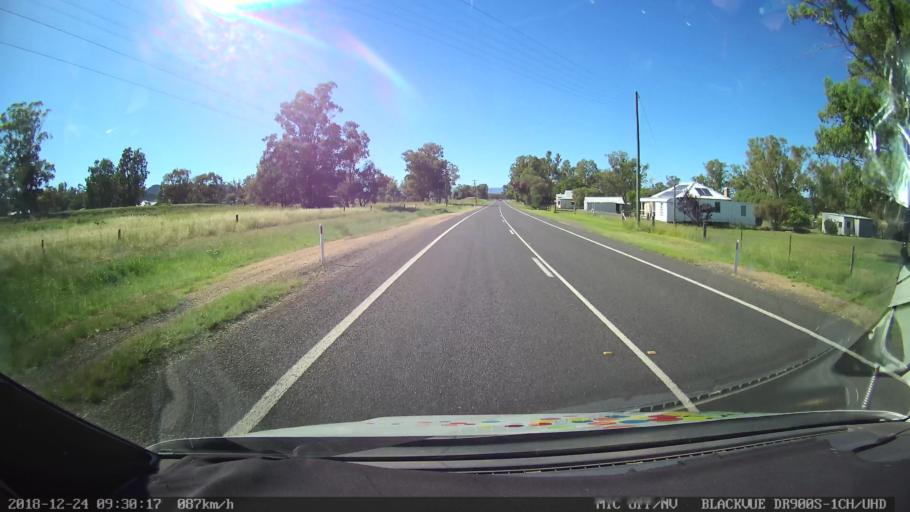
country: AU
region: New South Wales
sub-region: Liverpool Plains
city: Quirindi
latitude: -31.5605
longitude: 150.6969
